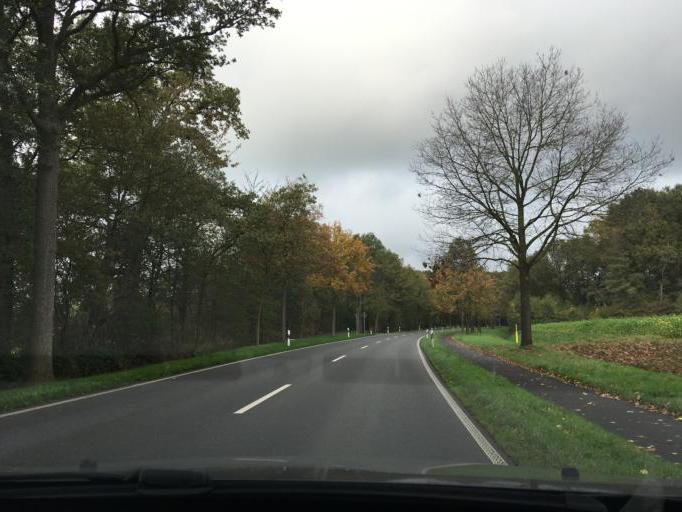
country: DE
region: North Rhine-Westphalia
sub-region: Regierungsbezirk Munster
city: Vreden
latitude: 52.0700
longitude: 6.7862
